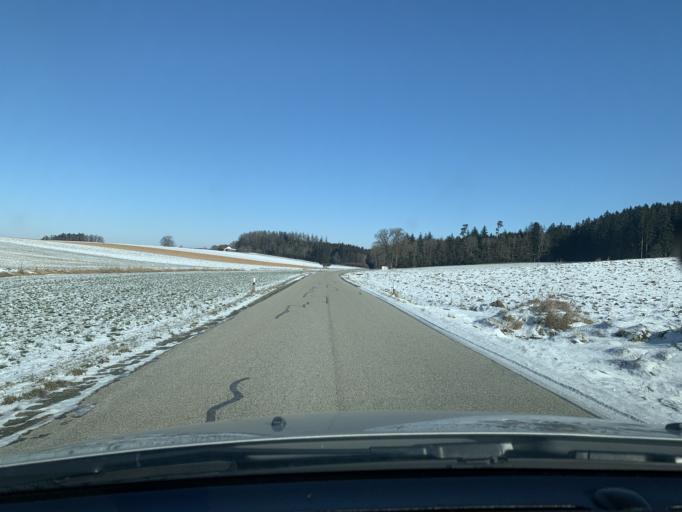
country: DE
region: Bavaria
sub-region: Upper Bavaria
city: Lohkirchen
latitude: 48.3154
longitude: 12.4507
